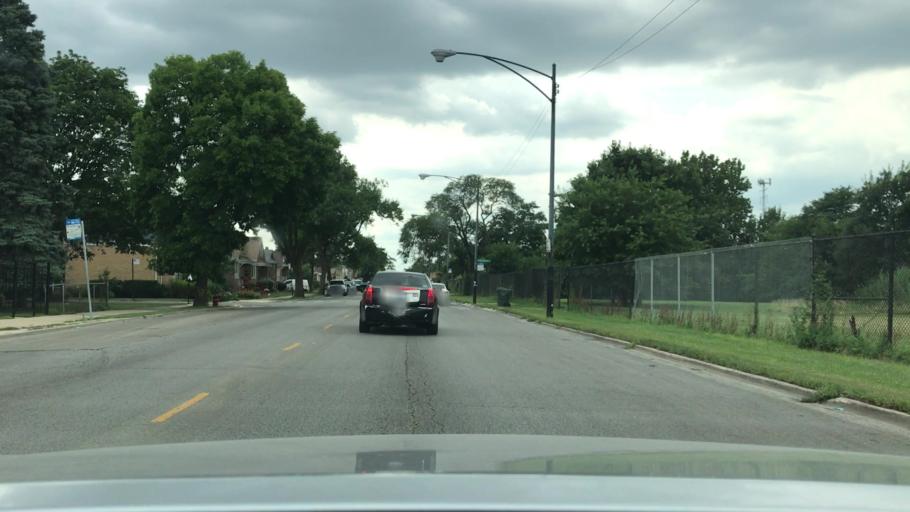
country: US
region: Illinois
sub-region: Cook County
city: Hometown
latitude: 41.7643
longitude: -87.7095
